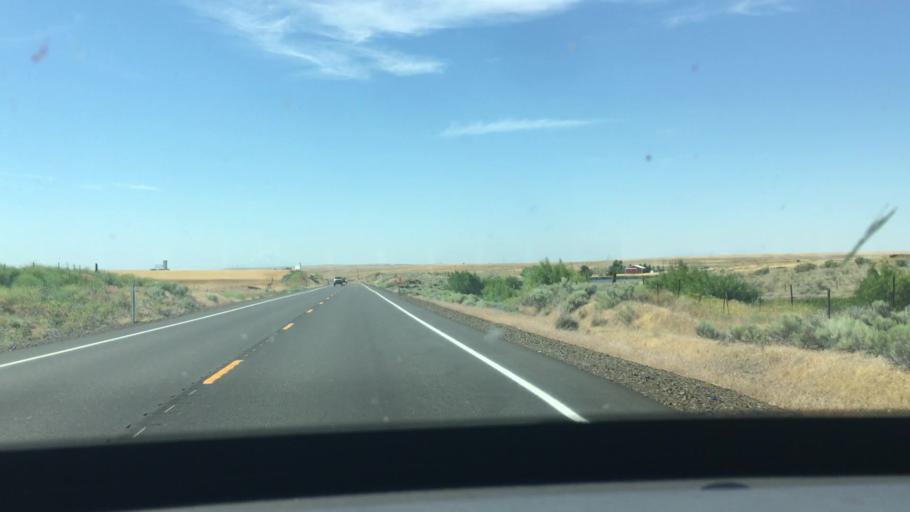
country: US
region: Oregon
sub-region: Sherman County
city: Moro
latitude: 45.3385
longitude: -120.7732
